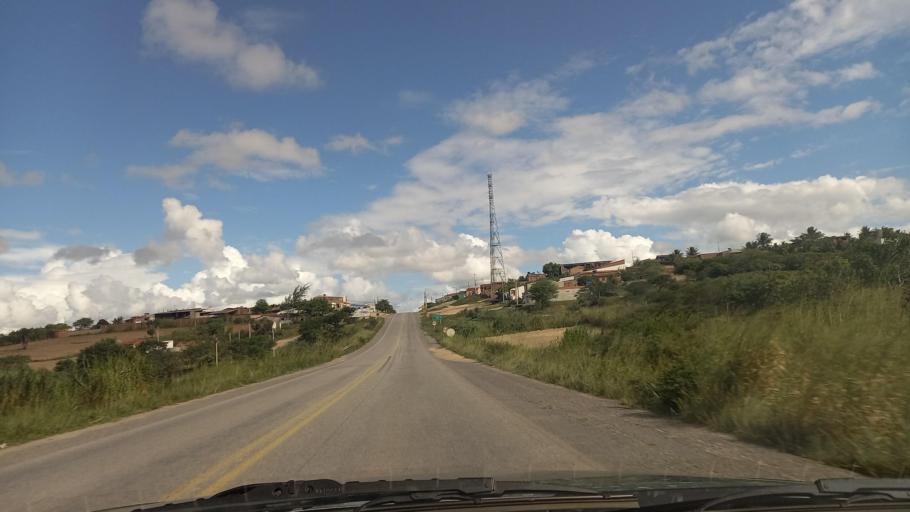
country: BR
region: Pernambuco
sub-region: Sao Joao
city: Sao Joao
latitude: -8.7504
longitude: -36.4311
